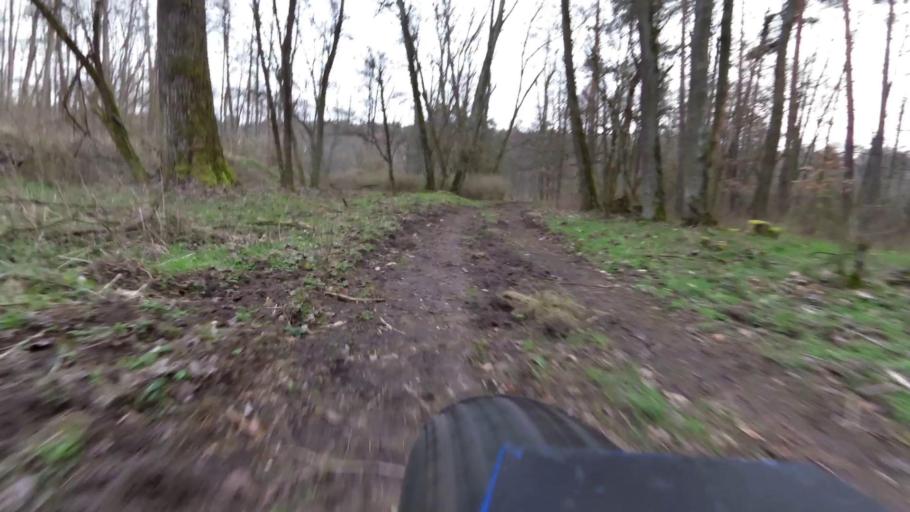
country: DE
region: Brandenburg
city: Ziltendorf
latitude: 52.2774
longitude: 14.6781
